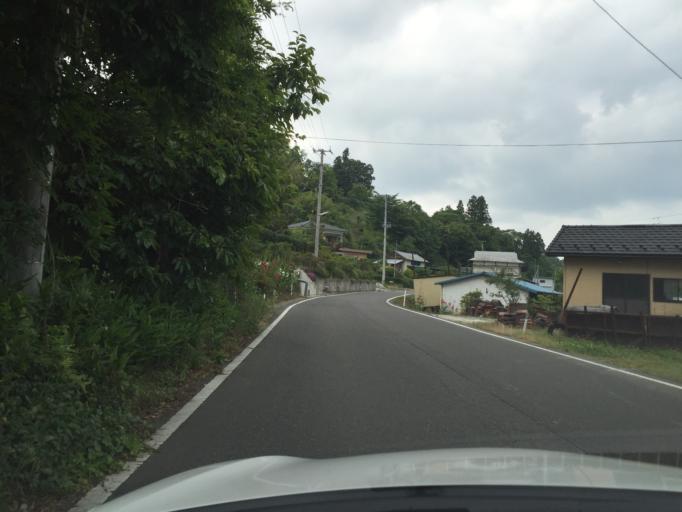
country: JP
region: Fukushima
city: Miharu
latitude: 37.3357
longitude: 140.4698
